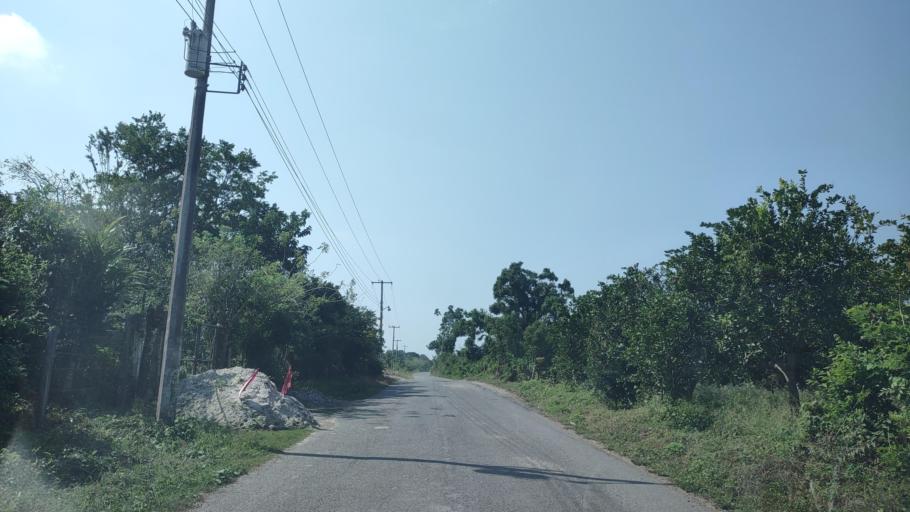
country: MX
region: Puebla
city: Espinal
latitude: 20.2594
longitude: -97.3180
